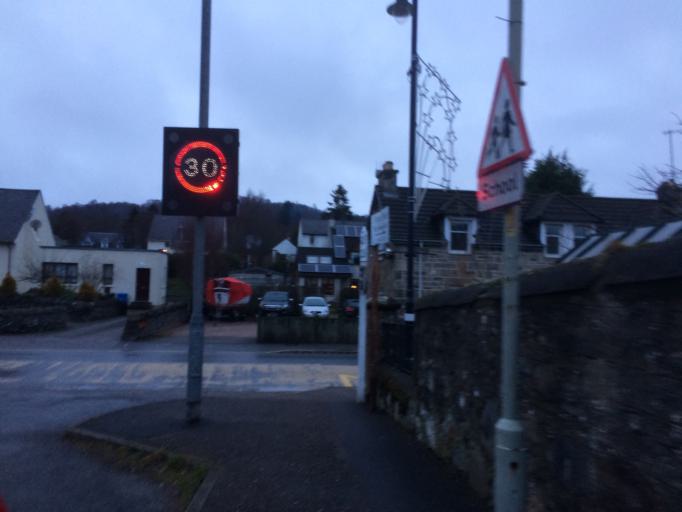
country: GB
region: Scotland
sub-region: Highland
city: Kingussie
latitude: 57.0656
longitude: -4.1186
